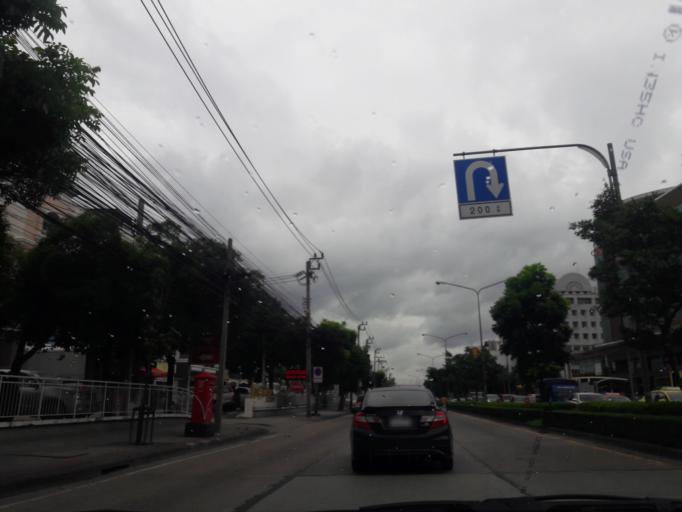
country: TH
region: Bangkok
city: Bueng Kum
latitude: 13.7979
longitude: 100.6501
